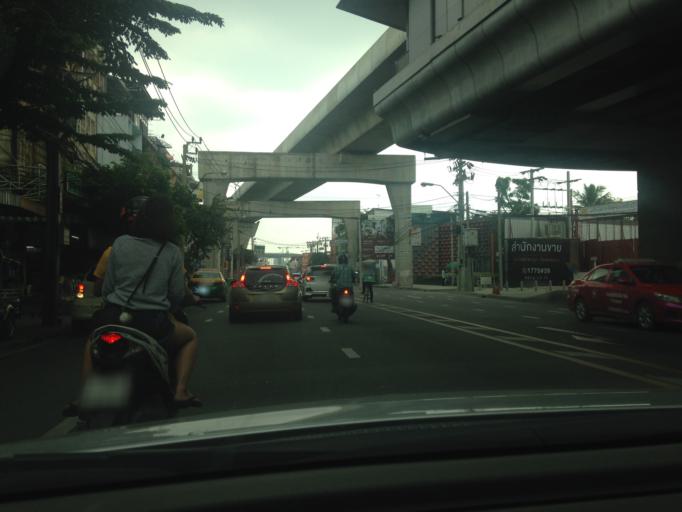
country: TH
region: Bangkok
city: Bang Sue
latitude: 13.8063
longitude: 100.5314
